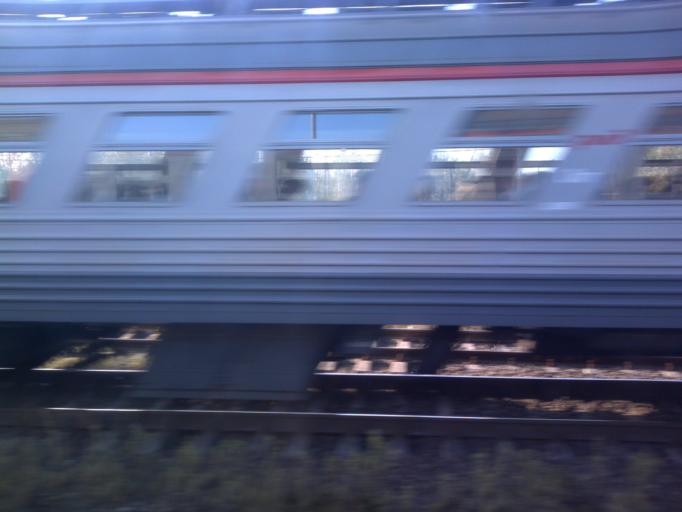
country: RU
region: St.-Petersburg
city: Krasnogvargeisky
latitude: 59.9816
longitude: 30.5101
